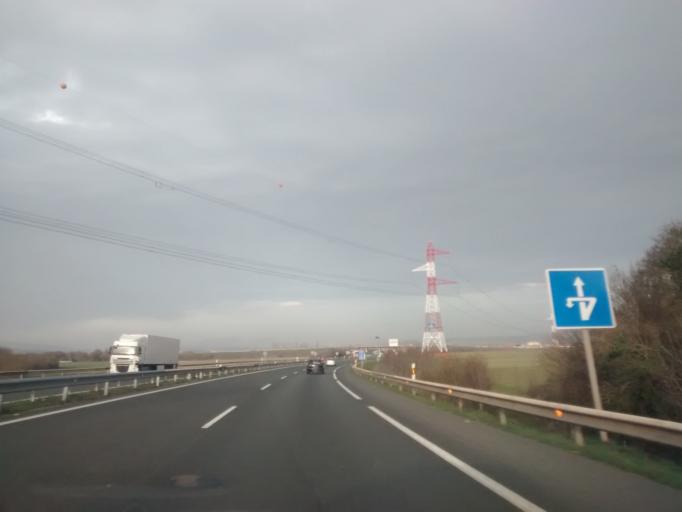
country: ES
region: Basque Country
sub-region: Provincia de Alava
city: Gasteiz / Vitoria
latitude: 42.8556
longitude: -2.7454
